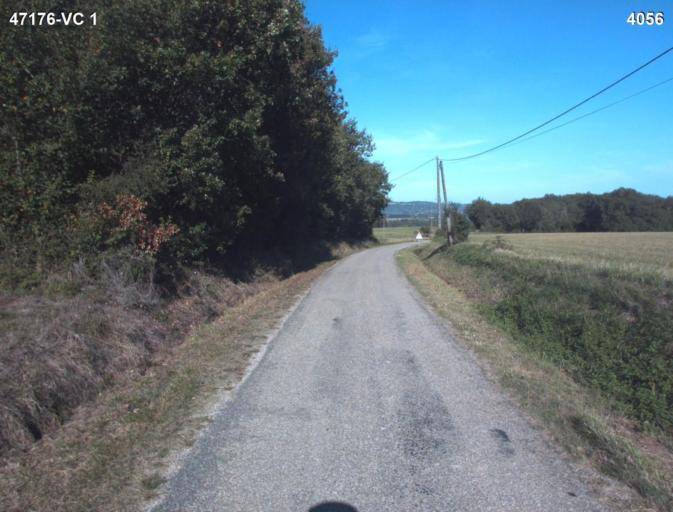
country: FR
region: Aquitaine
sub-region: Departement du Lot-et-Garonne
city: Vianne
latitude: 44.2222
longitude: 0.3126
